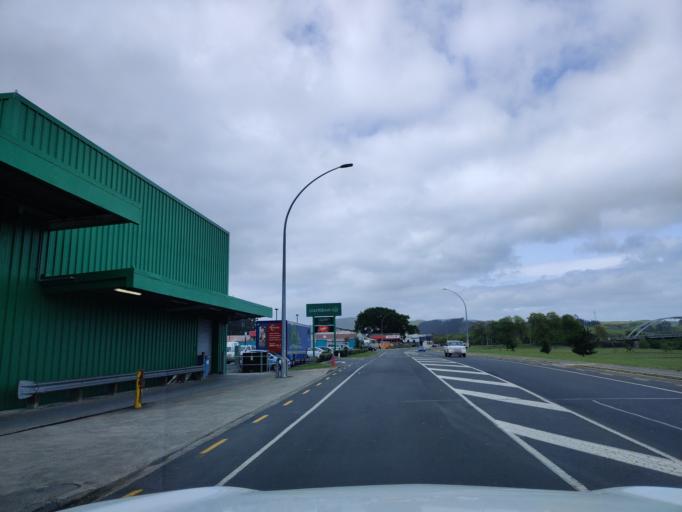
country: NZ
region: Waikato
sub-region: Waikato District
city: Ngaruawahia
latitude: -37.5641
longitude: 175.1584
